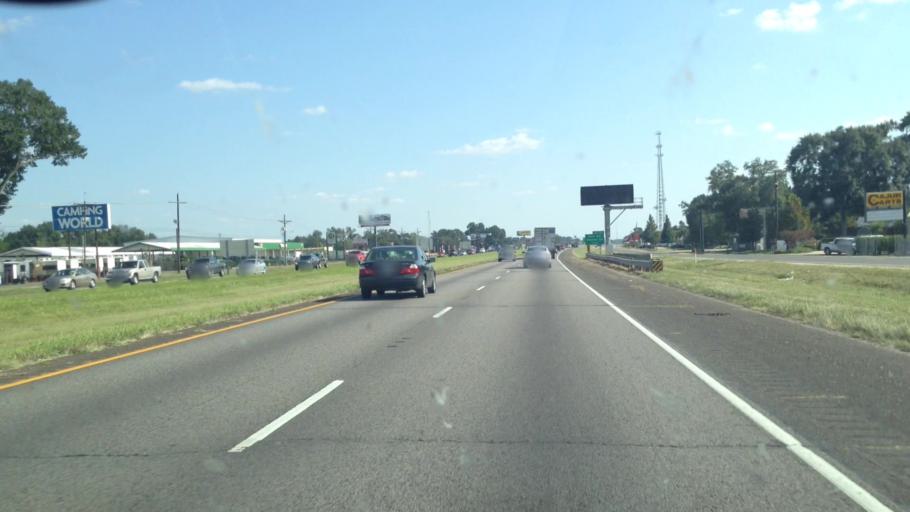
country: US
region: Louisiana
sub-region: Lafayette Parish
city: Carencro
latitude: 30.2870
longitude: -92.0224
